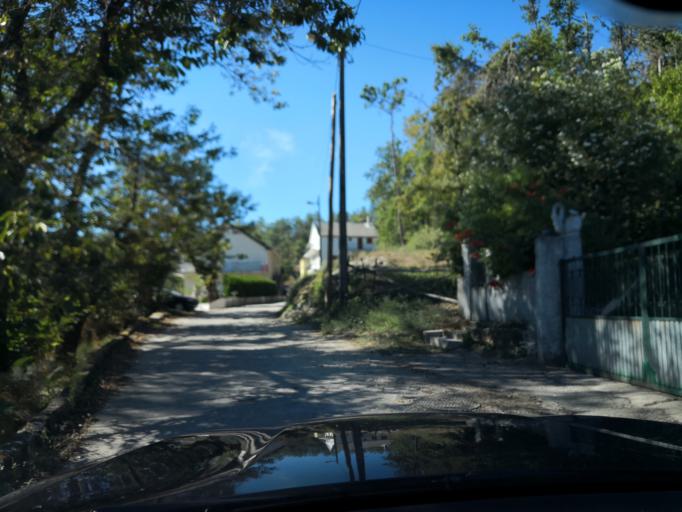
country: PT
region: Vila Real
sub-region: Santa Marta de Penaguiao
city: Santa Marta de Penaguiao
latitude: 41.2946
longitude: -7.8584
